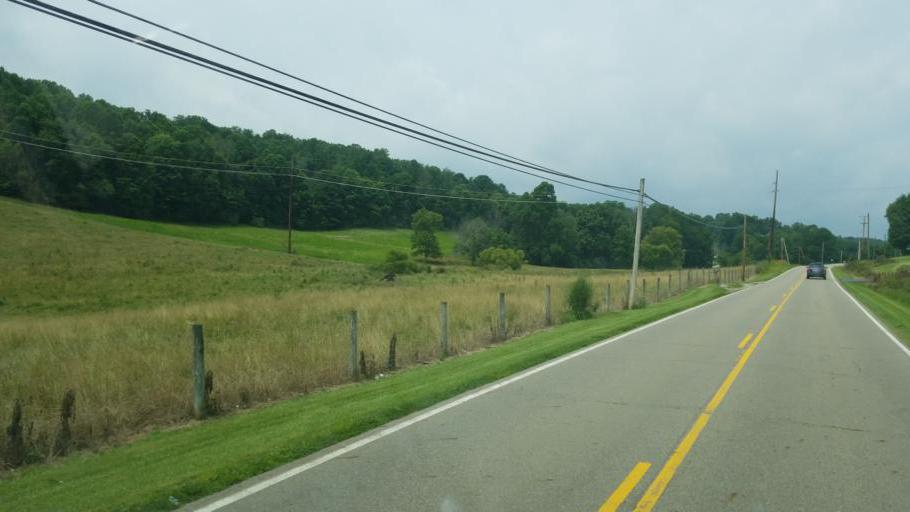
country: US
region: Ohio
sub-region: Licking County
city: Granville
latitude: 40.1398
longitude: -82.4693
